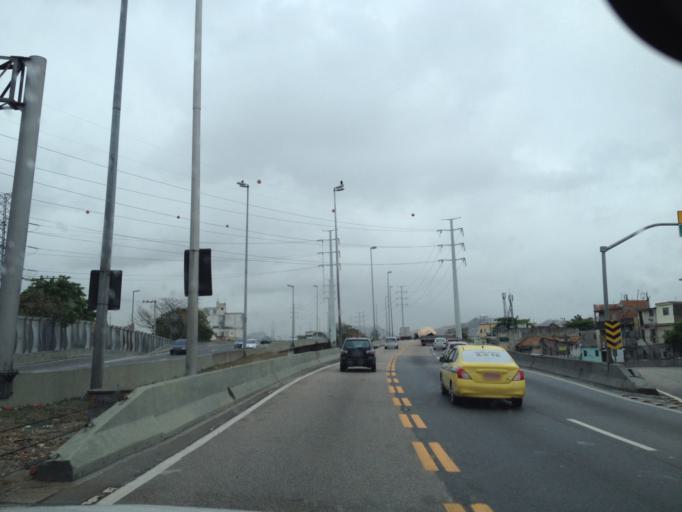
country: BR
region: Rio de Janeiro
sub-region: Rio De Janeiro
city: Rio de Janeiro
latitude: -22.8718
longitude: -43.2560
